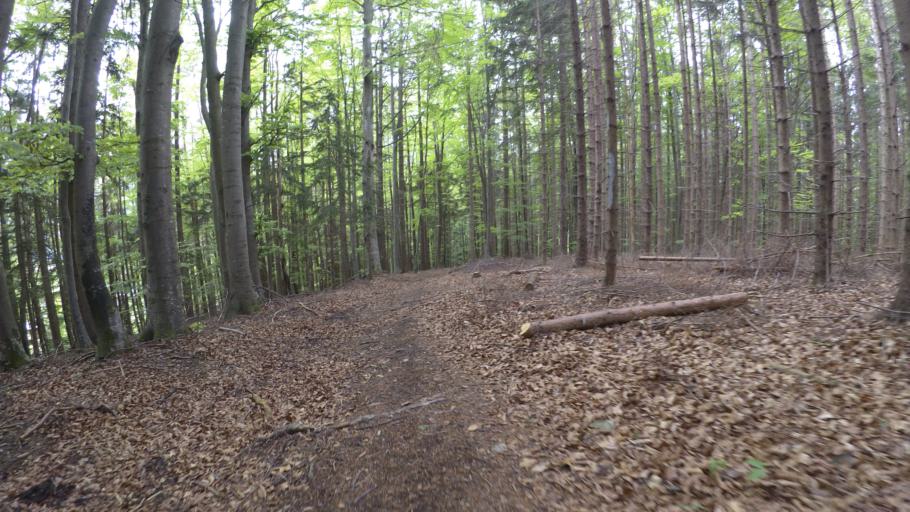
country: DE
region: Bavaria
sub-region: Upper Bavaria
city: Vachendorf
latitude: 47.8310
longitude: 12.6091
